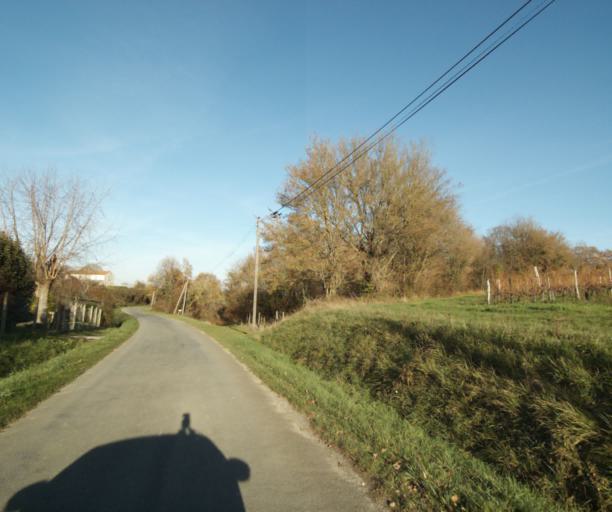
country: FR
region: Poitou-Charentes
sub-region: Departement de la Charente-Maritime
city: Burie
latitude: 45.7794
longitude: -0.4192
